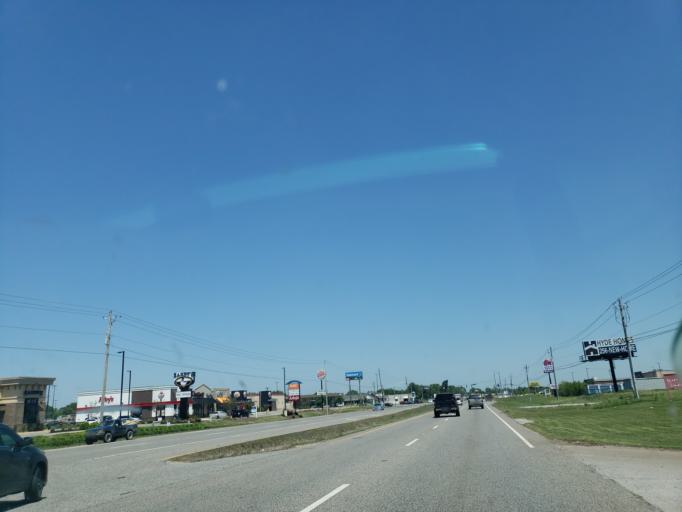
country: US
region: Alabama
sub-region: Madison County
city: Hazel Green
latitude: 34.9445
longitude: -86.5716
